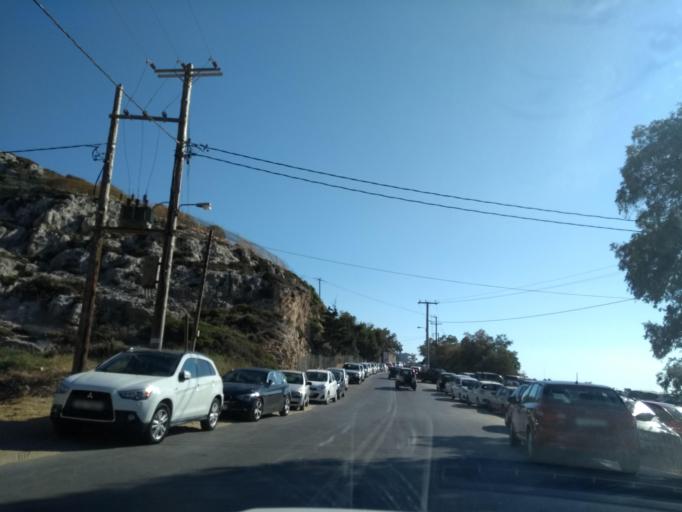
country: GR
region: Crete
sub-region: Nomos Chanias
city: Pithari
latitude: 35.5540
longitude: 24.0878
